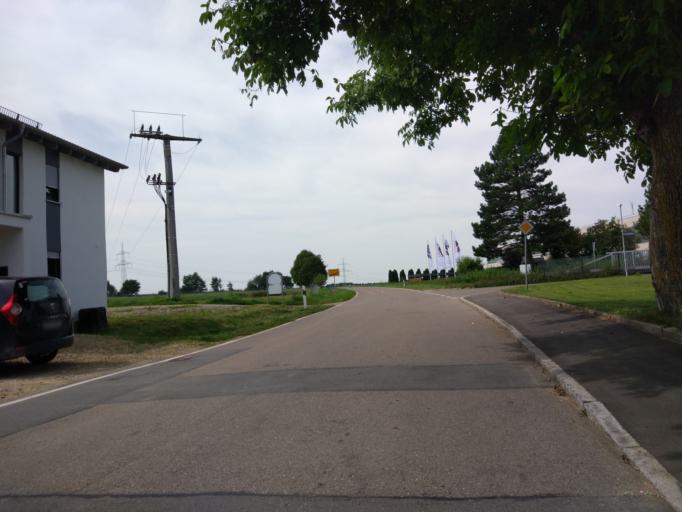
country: DE
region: Baden-Wuerttemberg
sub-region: Tuebingen Region
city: Huttisheim
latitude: 48.2817
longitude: 9.9359
